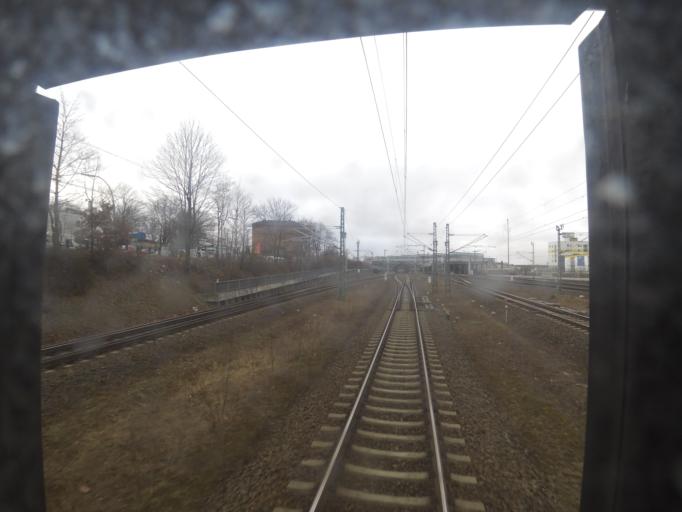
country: DE
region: Berlin
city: Berlin Schoeneberg
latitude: 52.4796
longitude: 13.3680
